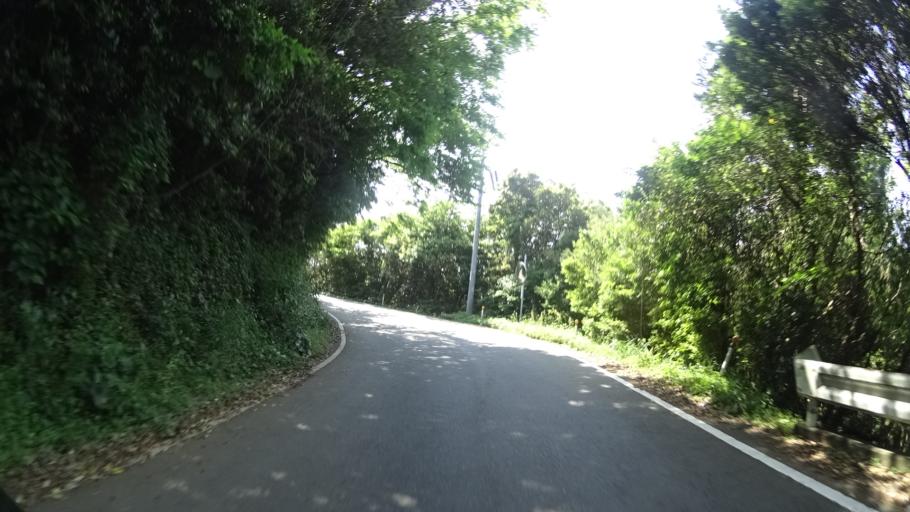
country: JP
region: Ehime
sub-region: Nishiuwa-gun
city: Ikata-cho
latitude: 33.3678
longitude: 132.0470
